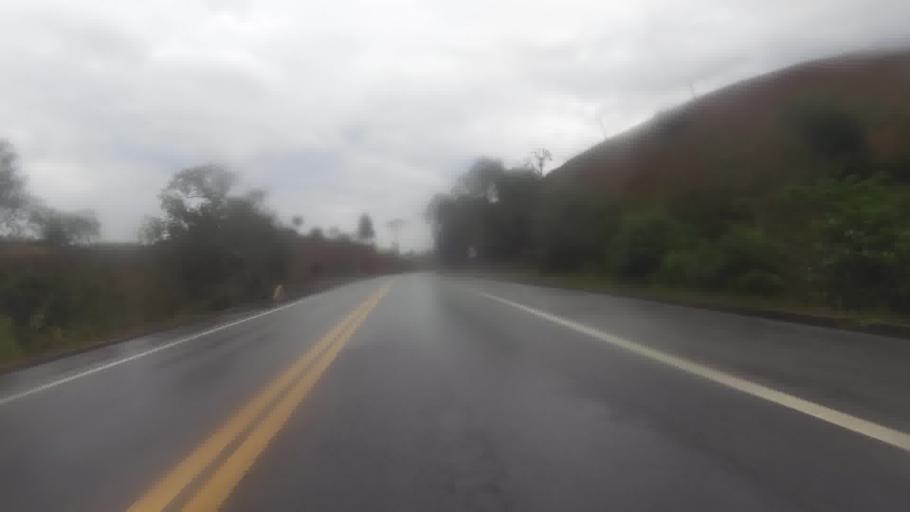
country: BR
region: Espirito Santo
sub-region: Cachoeiro De Itapemirim
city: Cachoeiro de Itapemirim
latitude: -21.0276
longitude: -41.1615
